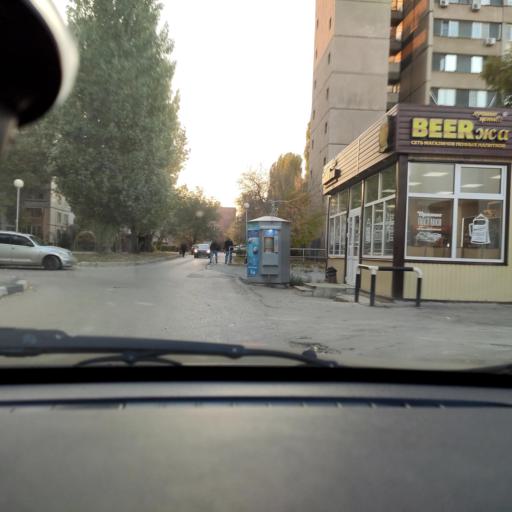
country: RU
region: Samara
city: Tol'yatti
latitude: 53.5284
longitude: 49.3116
